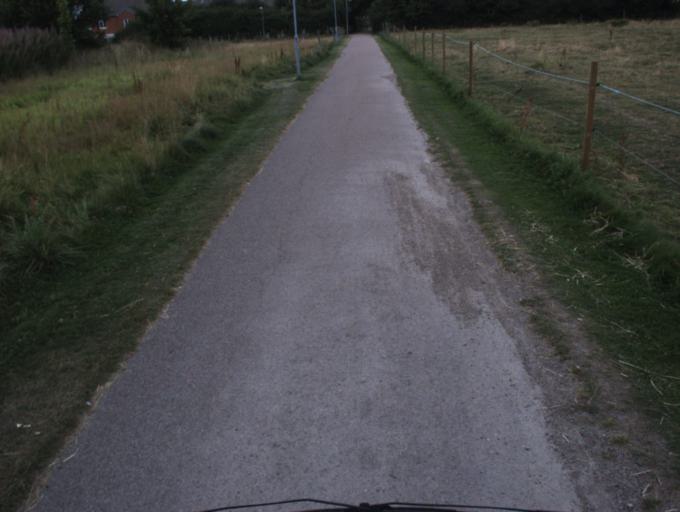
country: SE
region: Skane
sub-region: Helsingborg
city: Helsingborg
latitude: 56.0928
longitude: 12.6605
